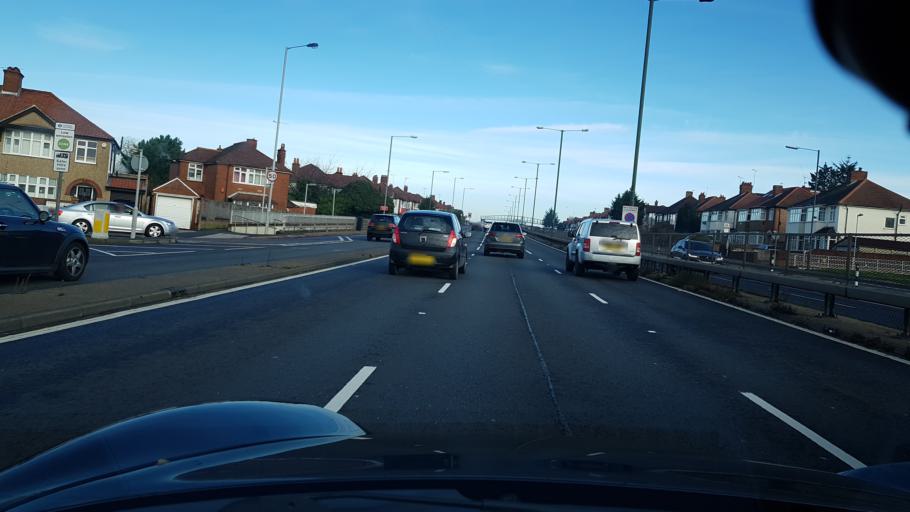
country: GB
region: England
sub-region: Greater London
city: Surbiton
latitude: 51.3824
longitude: -0.2774
